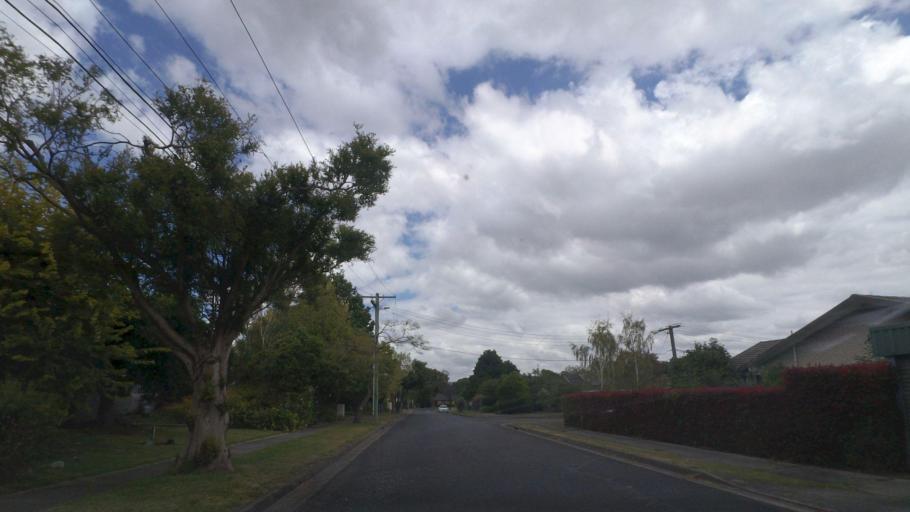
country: AU
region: Victoria
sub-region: Knox
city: Boronia
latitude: -37.8638
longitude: 145.2934
